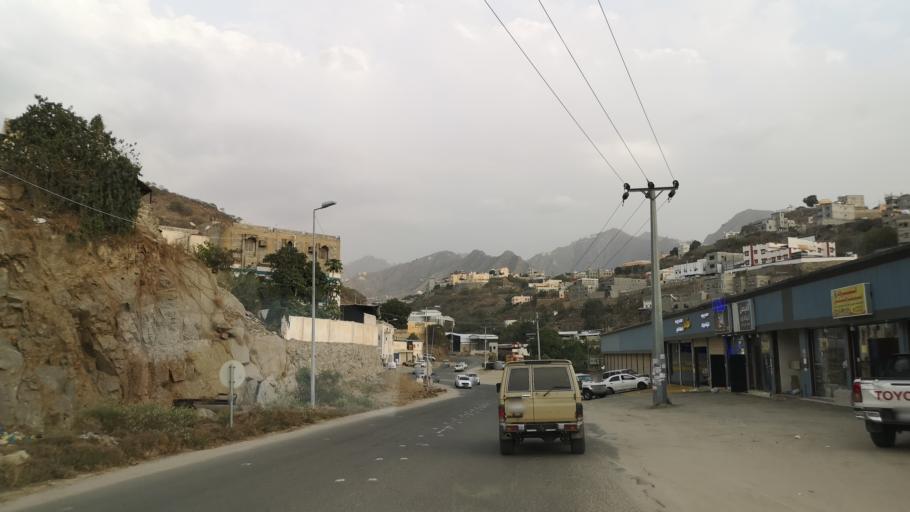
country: YE
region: Sa'dah
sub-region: Monabbih
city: Suq al Khamis
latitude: 17.3502
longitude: 43.1362
